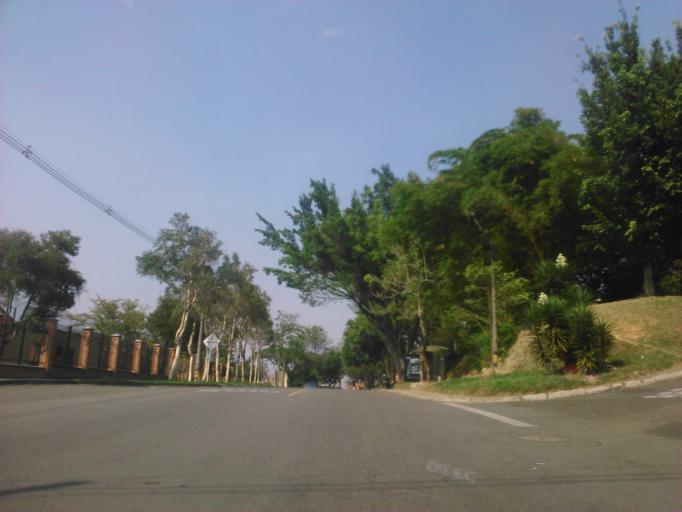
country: CO
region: Antioquia
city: Medellin
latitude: 6.2520
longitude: -75.6176
